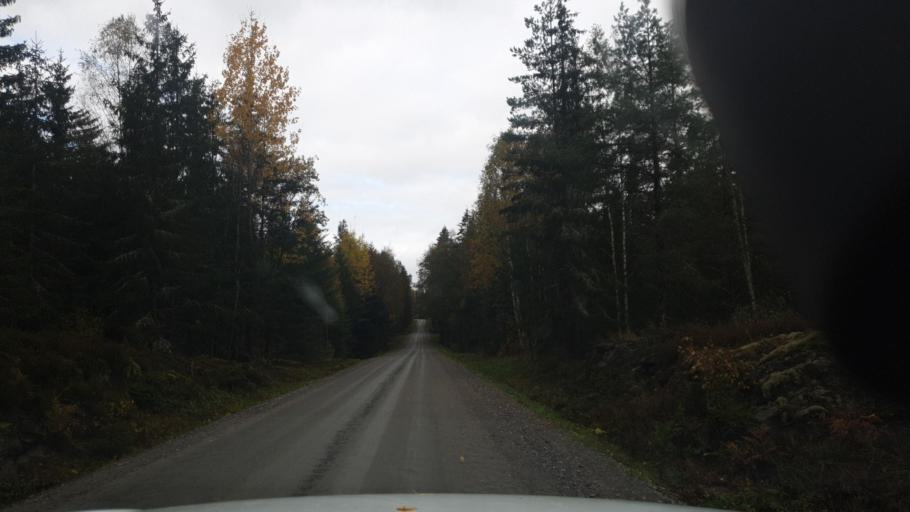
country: SE
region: Vaermland
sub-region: Karlstads Kommun
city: Valberg
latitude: 59.4497
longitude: 13.1069
